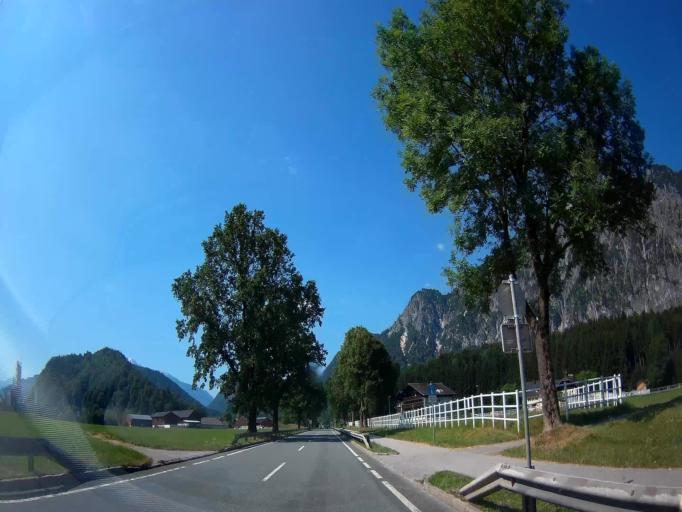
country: AT
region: Salzburg
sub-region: Politischer Bezirk Salzburg-Umgebung
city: Grodig
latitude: 47.7290
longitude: 13.0429
